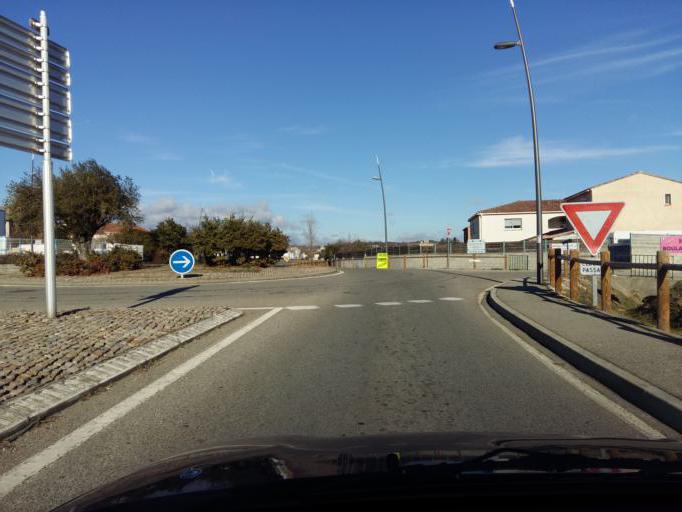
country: FR
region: Rhone-Alpes
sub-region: Departement de l'Ardeche
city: Saint-Just-d'Ardeche
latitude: 44.3076
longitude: 4.6134
